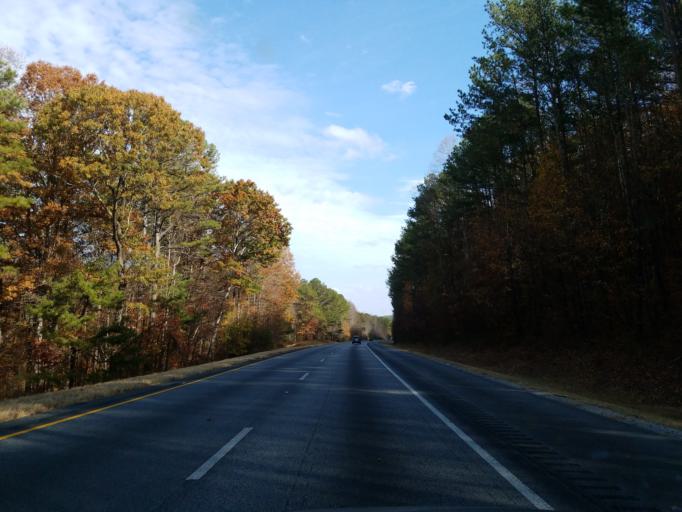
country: US
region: Alabama
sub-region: Cleburne County
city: Heflin
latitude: 33.6189
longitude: -85.6328
